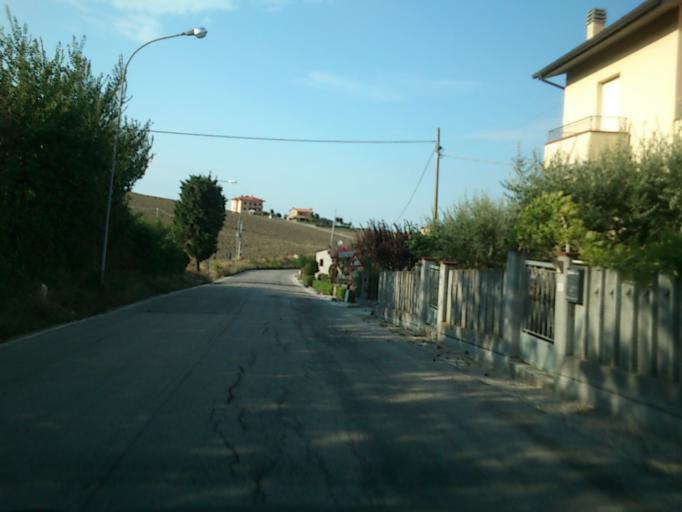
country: IT
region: The Marches
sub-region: Provincia di Pesaro e Urbino
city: San Costanzo
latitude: 43.7791
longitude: 13.0760
